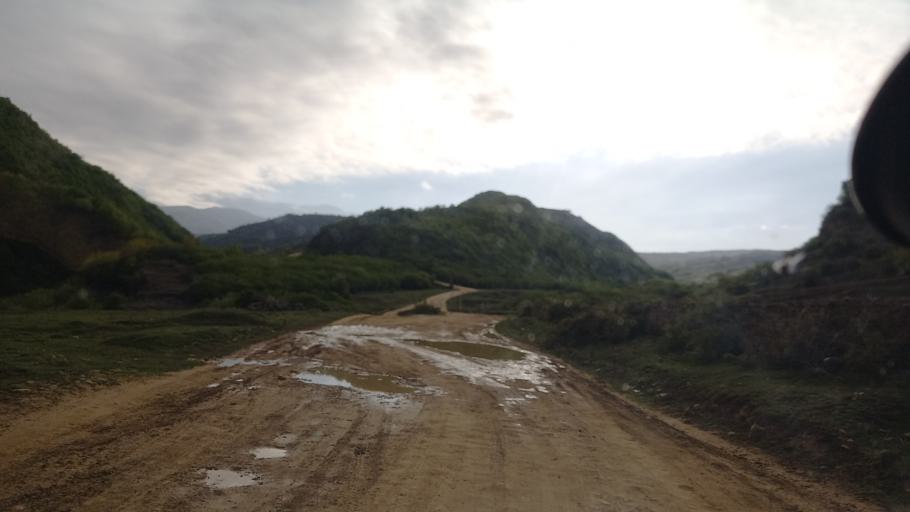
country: RU
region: Dagestan
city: Khuchni
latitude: 41.9617
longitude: 47.8671
